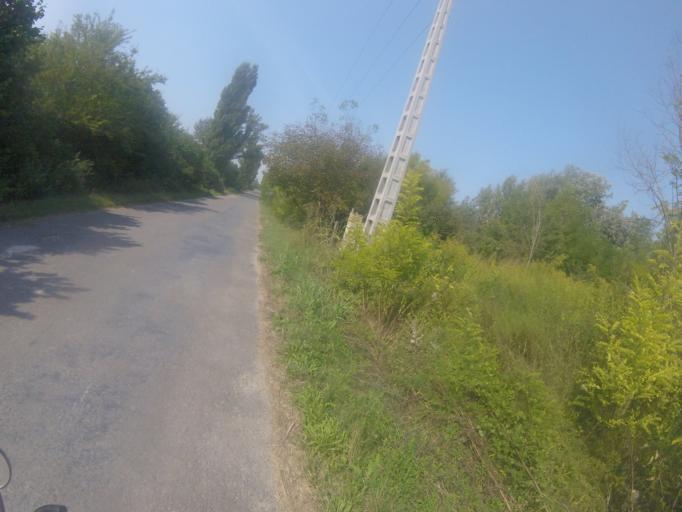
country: HU
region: Bacs-Kiskun
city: Ersekcsanad
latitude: 46.2570
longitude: 18.9303
